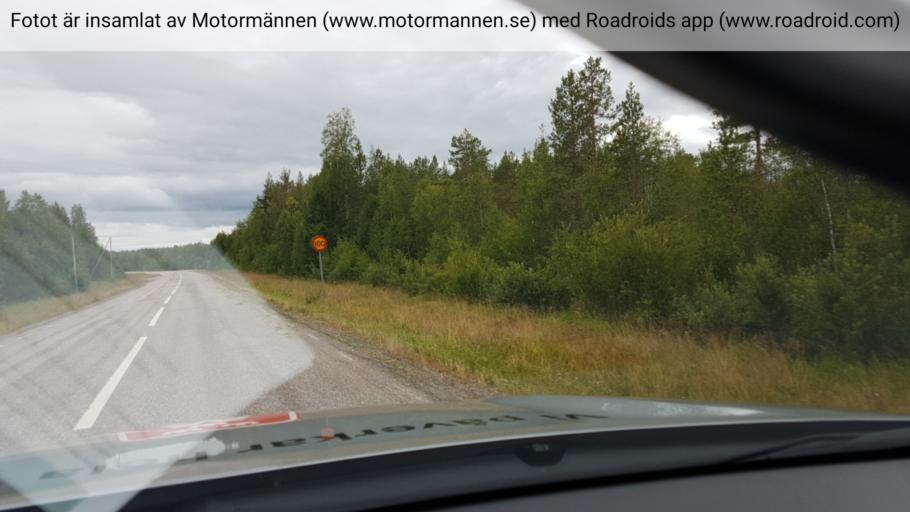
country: SE
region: Norrbotten
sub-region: Overkalix Kommun
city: OEverkalix
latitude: 66.7792
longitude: 22.9072
